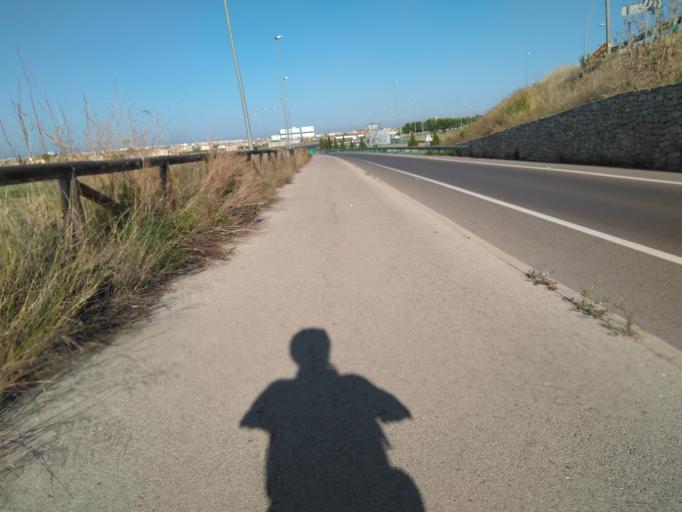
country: ES
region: Valencia
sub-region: Provincia de Valencia
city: Burjassot
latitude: 39.5033
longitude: -0.3960
